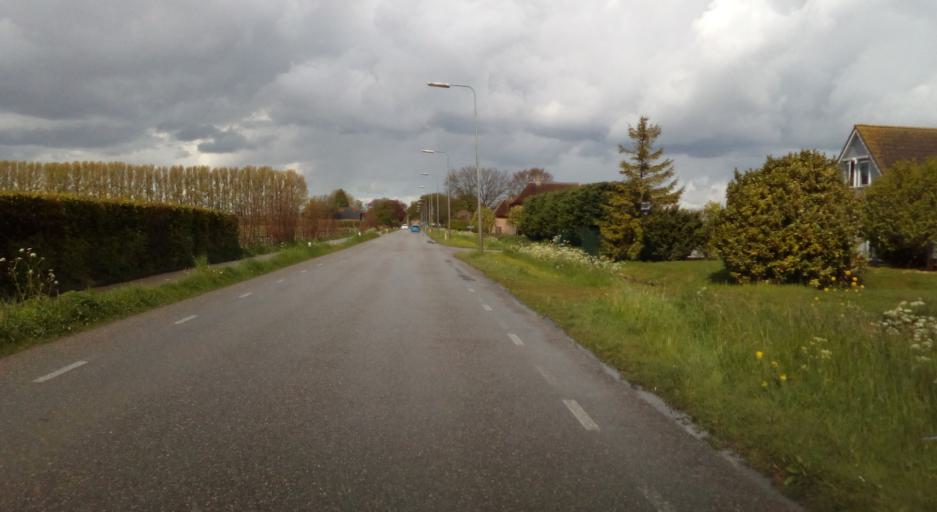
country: NL
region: South Holland
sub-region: Gemeente Zwijndrecht
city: Zwijndrecht
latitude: 51.8359
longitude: 4.6078
